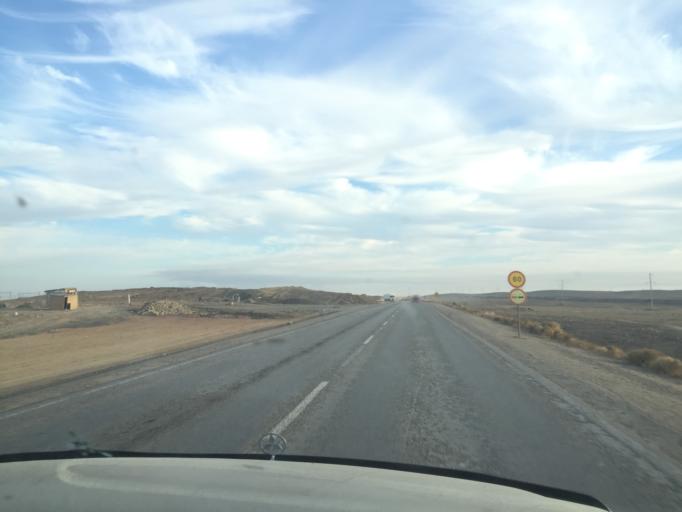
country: KZ
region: Almaty Oblysy
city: Ulken
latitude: 45.1856
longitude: 73.9197
